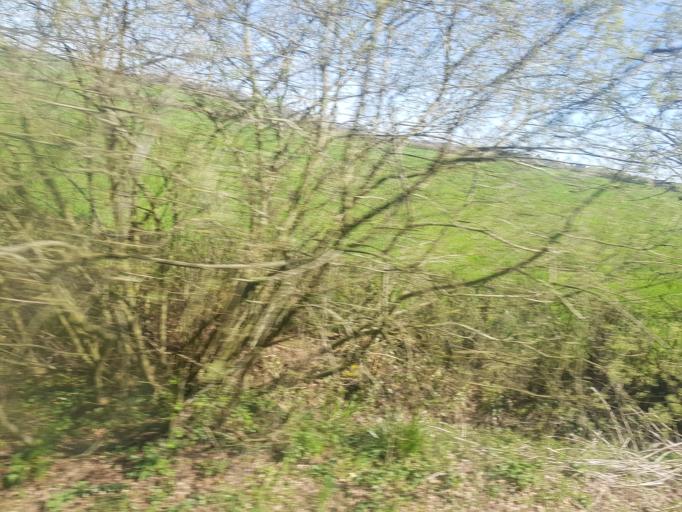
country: GB
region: England
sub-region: Isle of Wight
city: Newport
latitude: 50.7262
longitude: -1.2620
